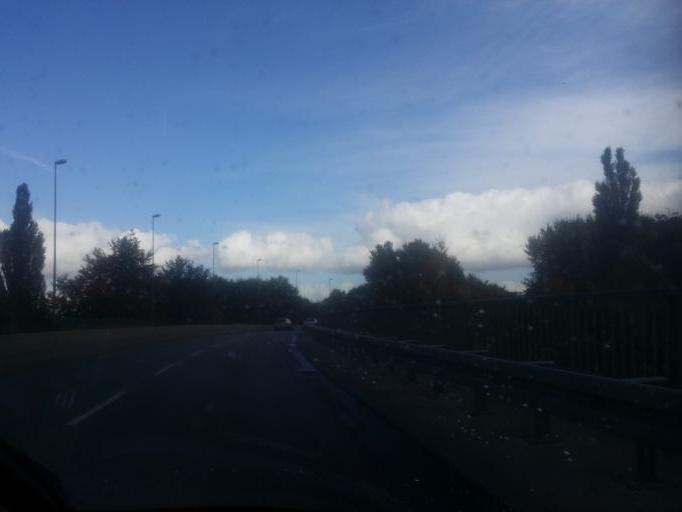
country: DE
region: Schleswig-Holstein
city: Pinneberg
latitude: 53.6619
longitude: 9.7868
